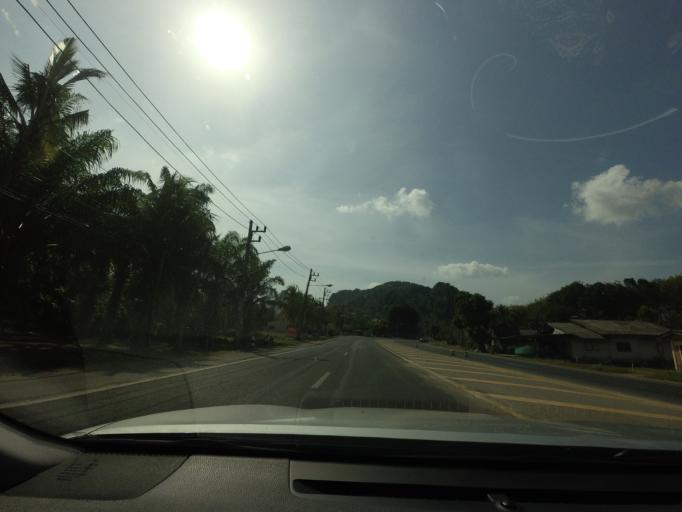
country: TH
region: Phangnga
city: Ban Ao Nang
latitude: 8.0947
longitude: 98.8056
